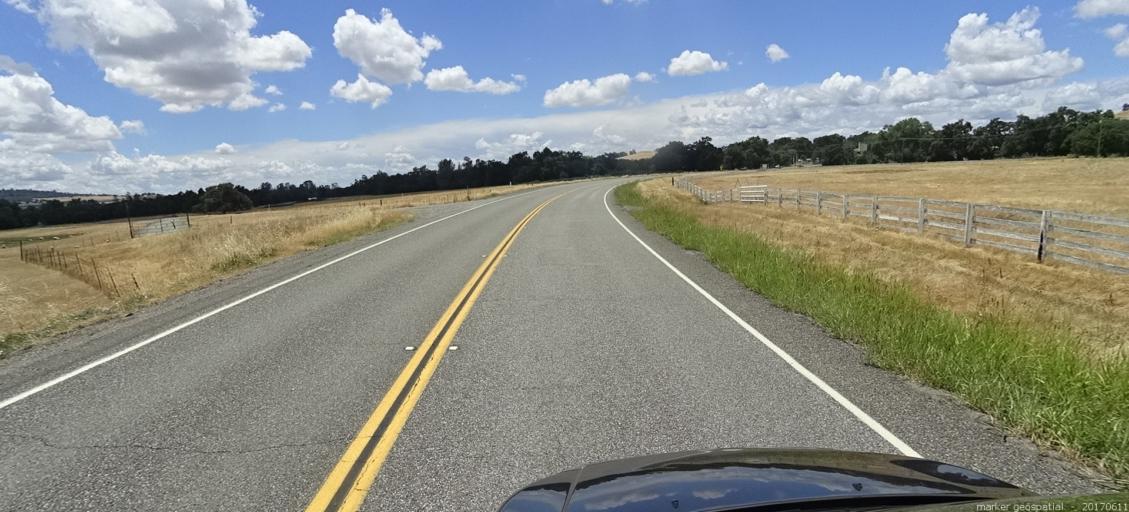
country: US
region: California
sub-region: Butte County
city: Paradise
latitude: 39.6535
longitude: -121.5851
